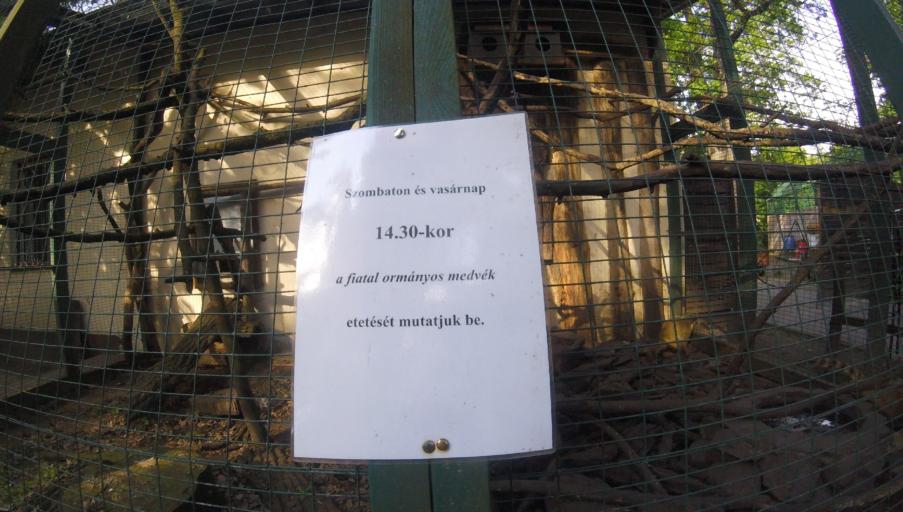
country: HU
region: Bacs-Kiskun
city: Kecskemet
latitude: 46.8979
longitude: 19.7161
